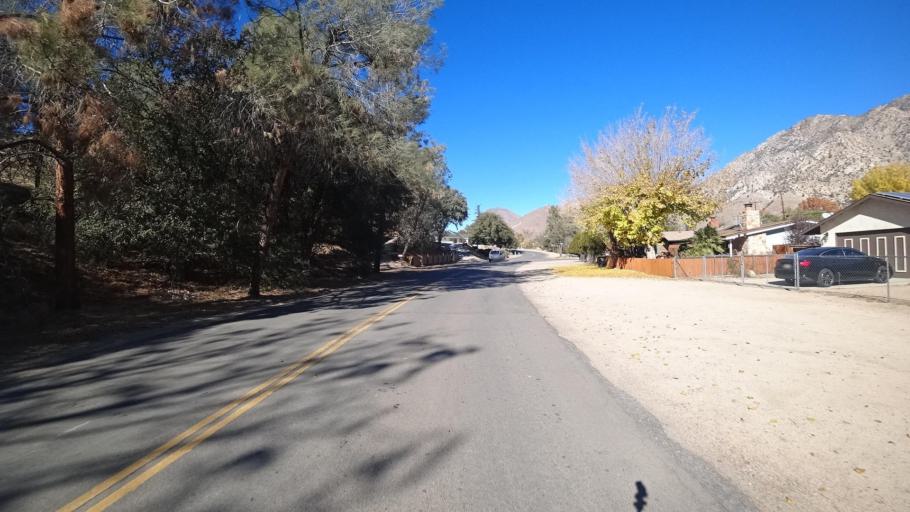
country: US
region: California
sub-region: Kern County
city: Kernville
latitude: 35.7558
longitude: -118.4287
